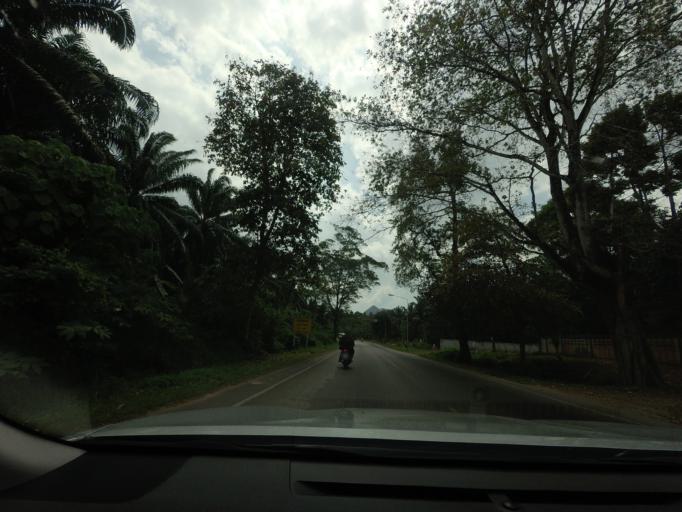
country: TH
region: Phangnga
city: Ban Ao Nang
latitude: 8.1139
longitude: 98.8022
